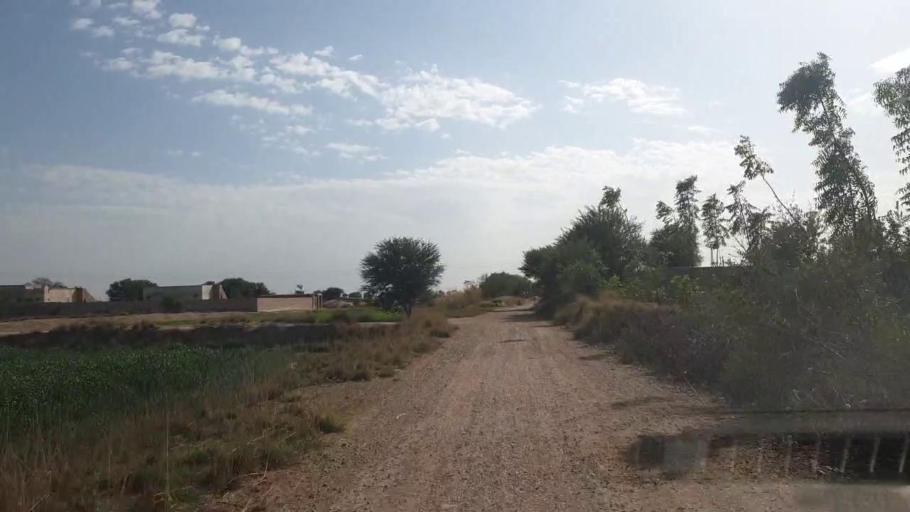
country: PK
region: Sindh
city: Shahdadpur
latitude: 26.0002
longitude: 68.4892
